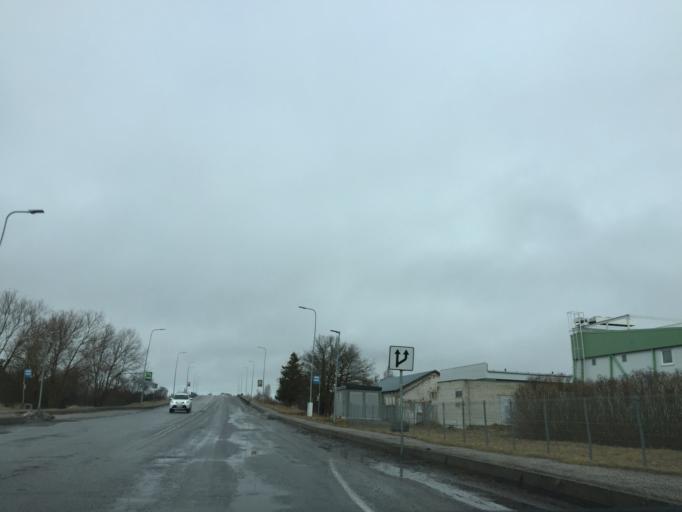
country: EE
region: Laeaene
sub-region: Haapsalu linn
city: Haapsalu
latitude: 58.9283
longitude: 23.5444
